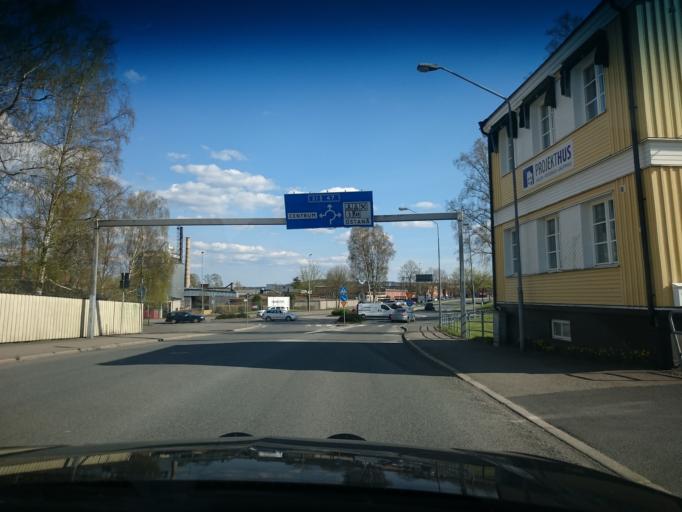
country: SE
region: Joenkoeping
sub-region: Vetlanda Kommun
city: Vetlanda
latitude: 57.4217
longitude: 15.0799
